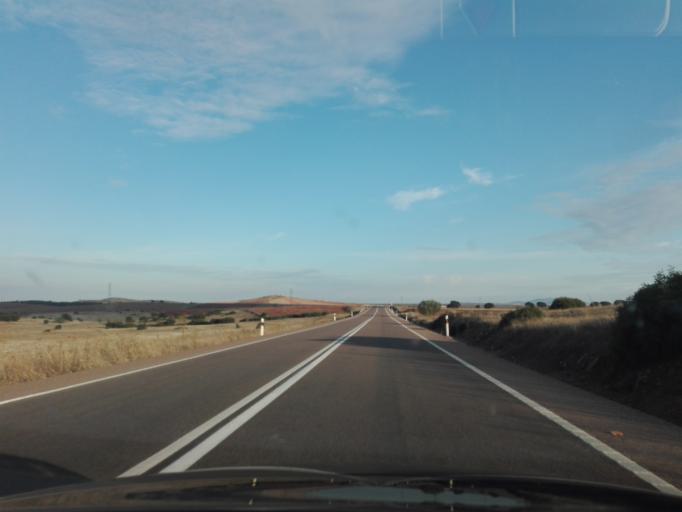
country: ES
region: Extremadura
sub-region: Provincia de Badajoz
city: Usagre
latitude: 38.3642
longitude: -6.2296
